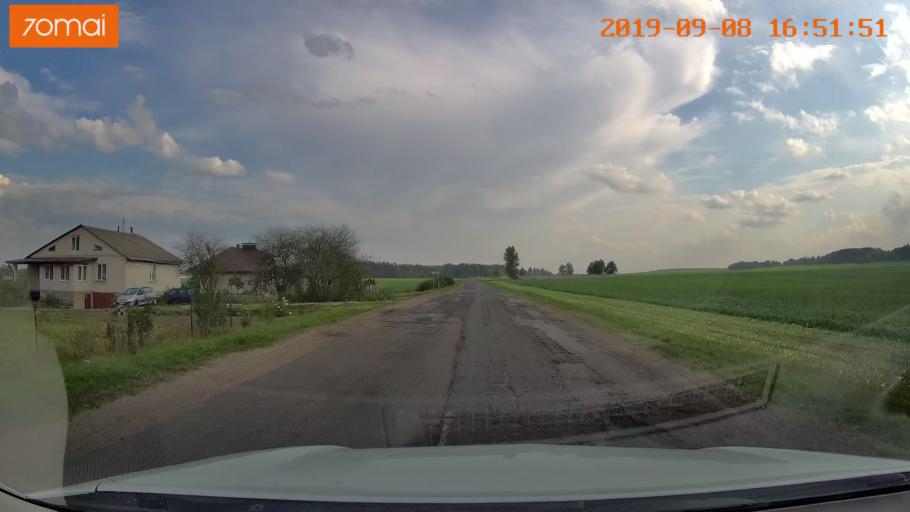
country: BY
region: Grodnenskaya
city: Hrodna
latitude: 53.7815
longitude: 23.8983
